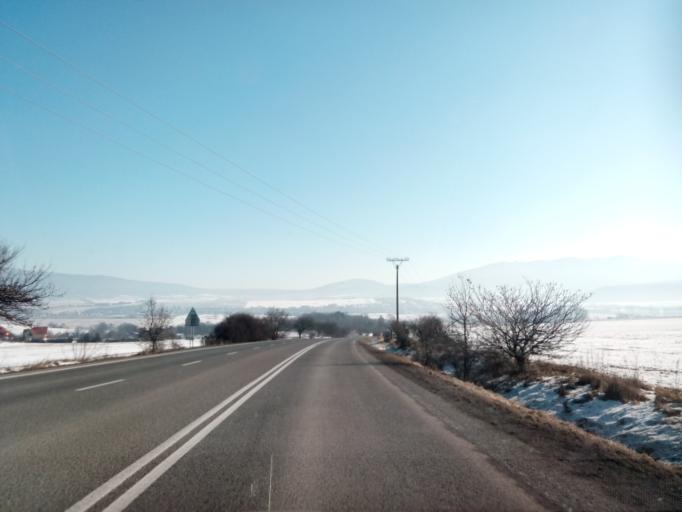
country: SK
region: Kosicky
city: Kosice
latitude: 48.7347
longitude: 21.4061
